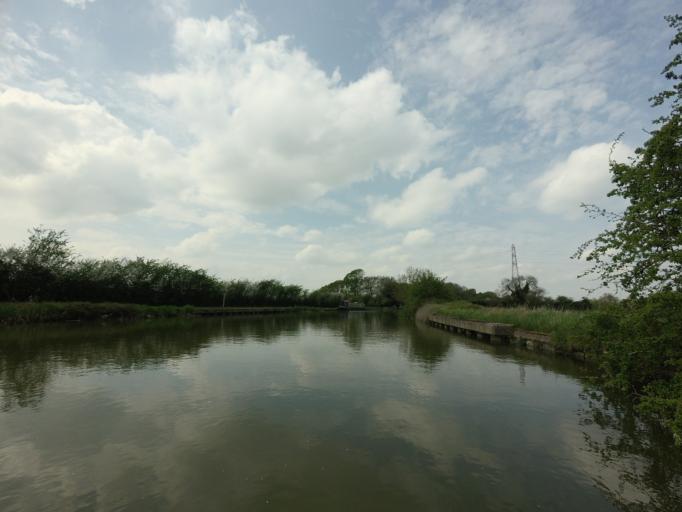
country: GB
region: England
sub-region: Central Bedfordshire
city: Leighton Buzzard
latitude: 51.8878
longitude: -0.6612
